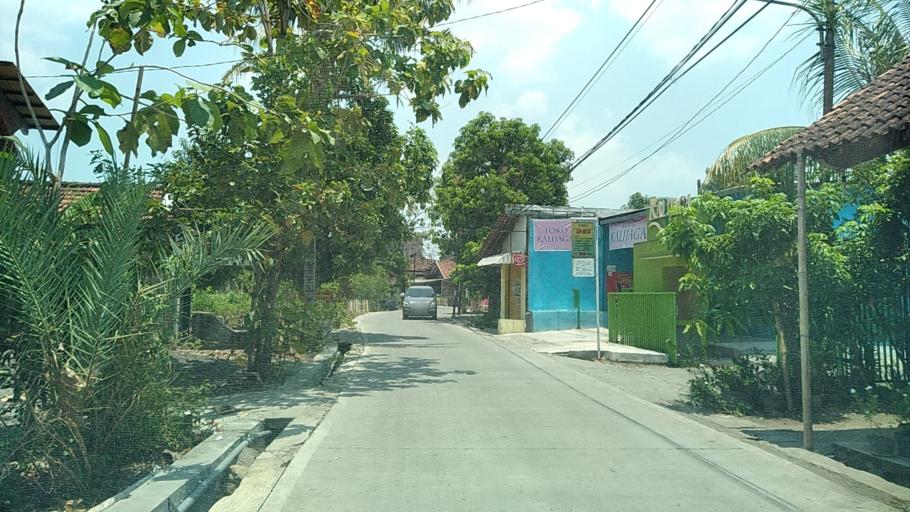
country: ID
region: Central Java
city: Mranggen
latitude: -7.0154
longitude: 110.4888
